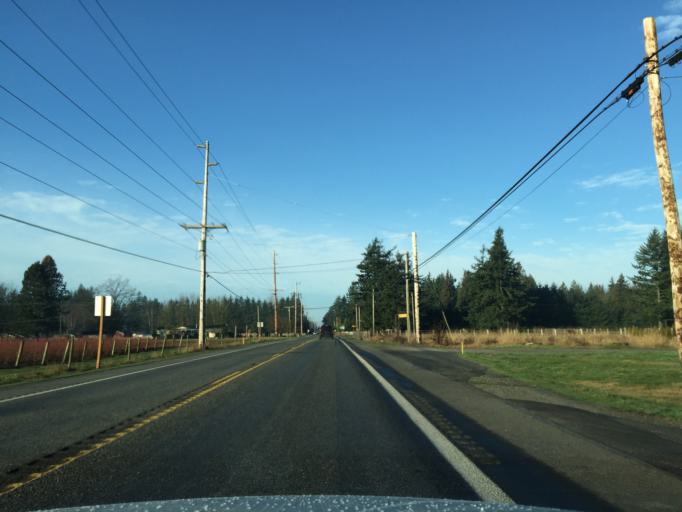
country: US
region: Washington
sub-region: Whatcom County
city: Lynden
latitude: 48.9353
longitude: -122.5277
